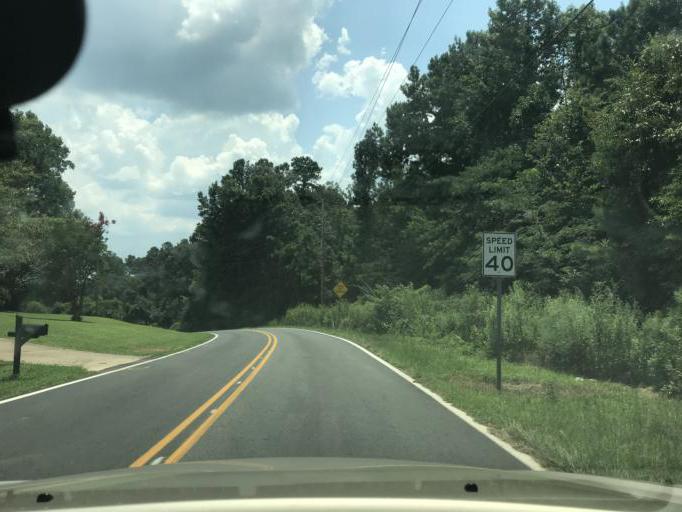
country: US
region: Georgia
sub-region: Forsyth County
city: Cumming
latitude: 34.2367
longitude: -84.2056
